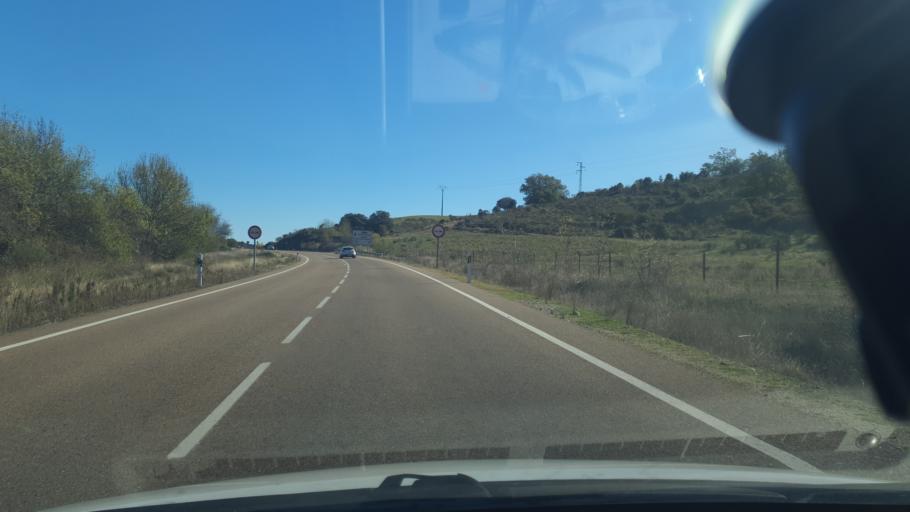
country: ES
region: Castille and Leon
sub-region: Provincia de Avila
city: Poyales del Hoyo
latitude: 40.1576
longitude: -5.1742
